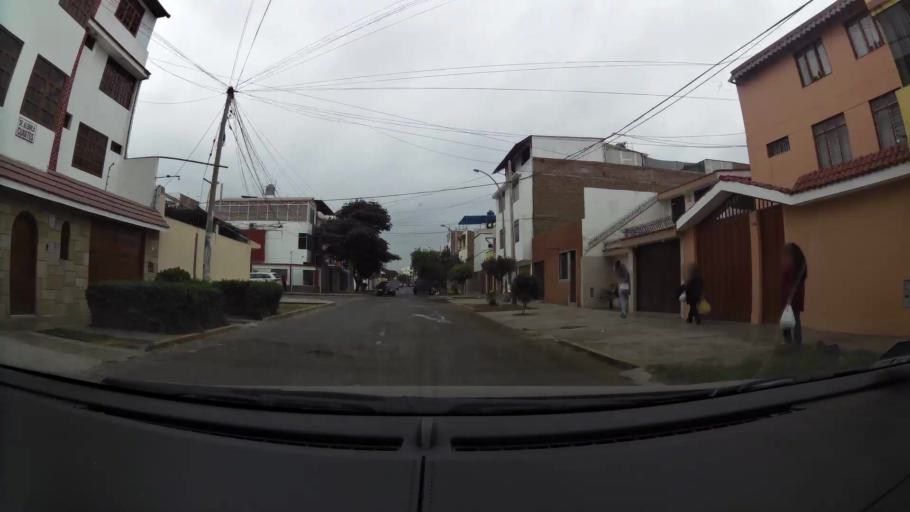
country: PE
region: La Libertad
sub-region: Provincia de Trujillo
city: Trujillo
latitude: -8.1206
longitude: -79.0310
